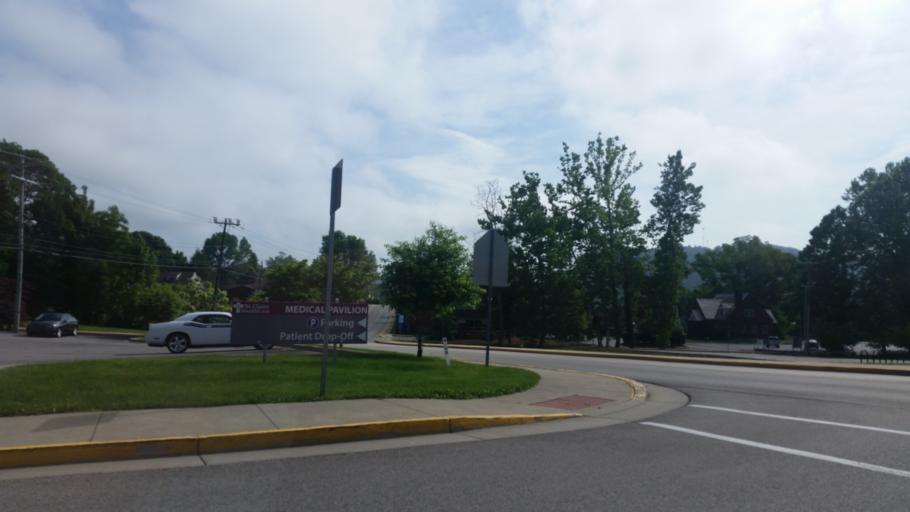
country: US
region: Kentucky
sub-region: Rowan County
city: Morehead
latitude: 38.1800
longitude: -83.4396
